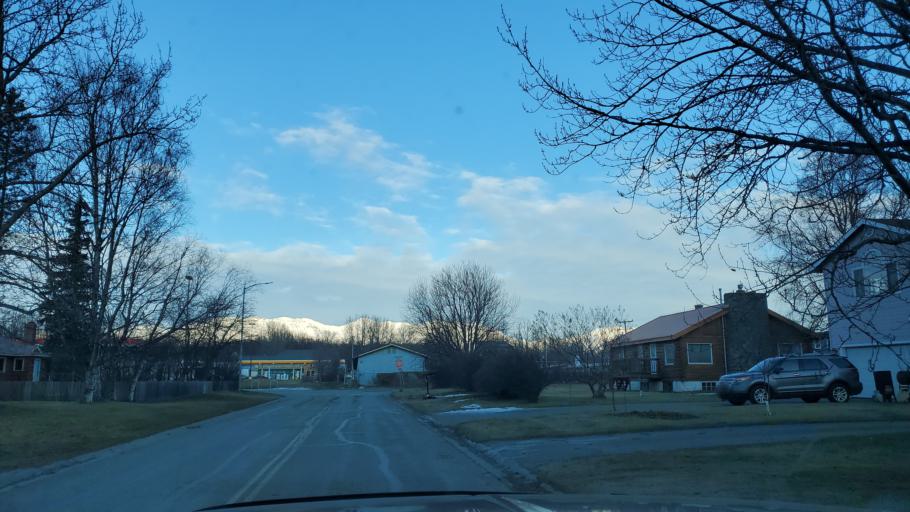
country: US
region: Alaska
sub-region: Matanuska-Susitna Borough
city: Palmer
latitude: 61.6051
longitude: -149.1165
